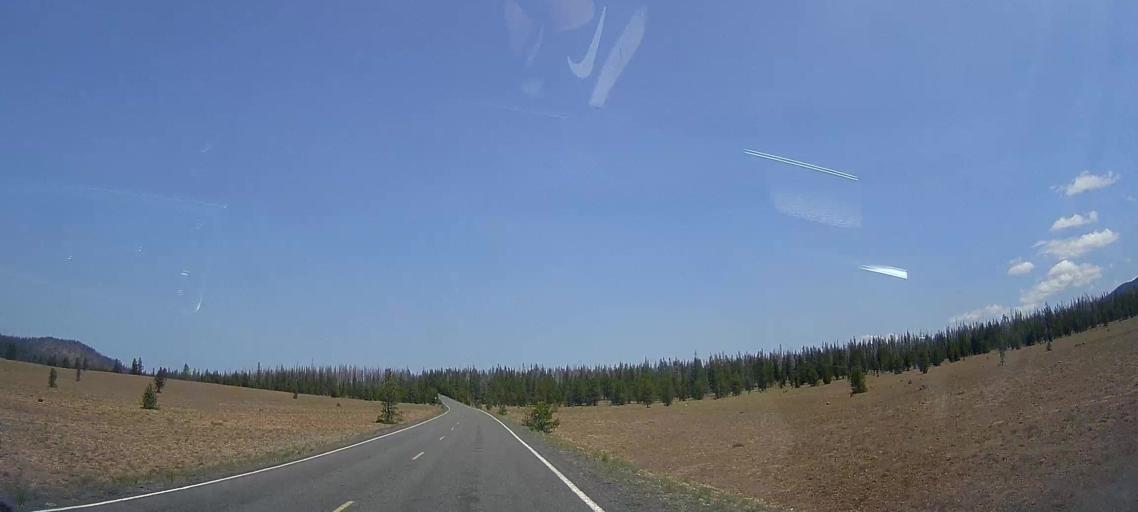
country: US
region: Oregon
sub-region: Lane County
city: Oakridge
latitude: 43.0325
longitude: -122.1176
